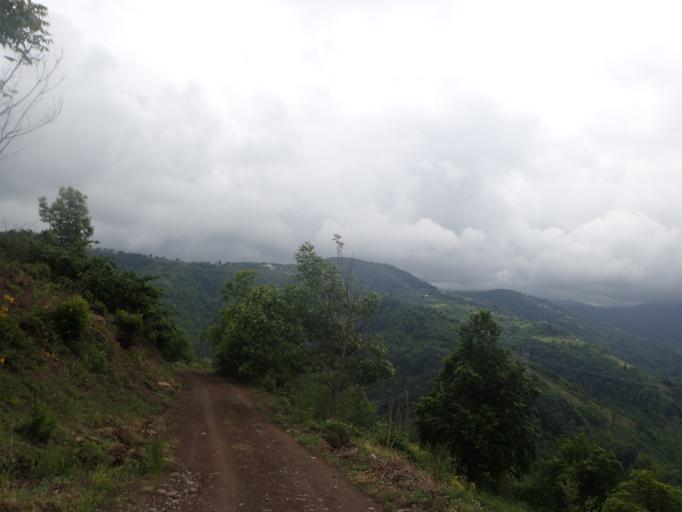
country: TR
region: Samsun
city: Salipazari
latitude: 40.9433
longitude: 36.8968
